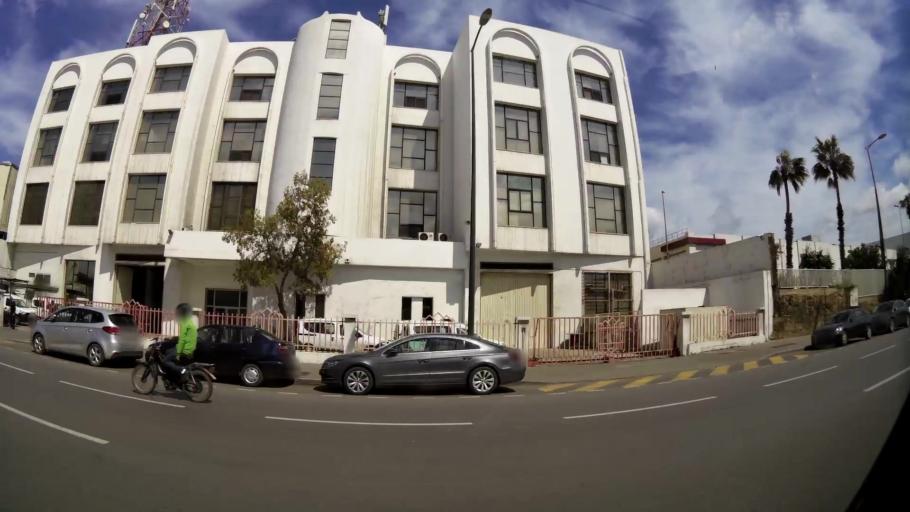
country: MA
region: Grand Casablanca
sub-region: Casablanca
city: Casablanca
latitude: 33.6027
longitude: -7.5519
